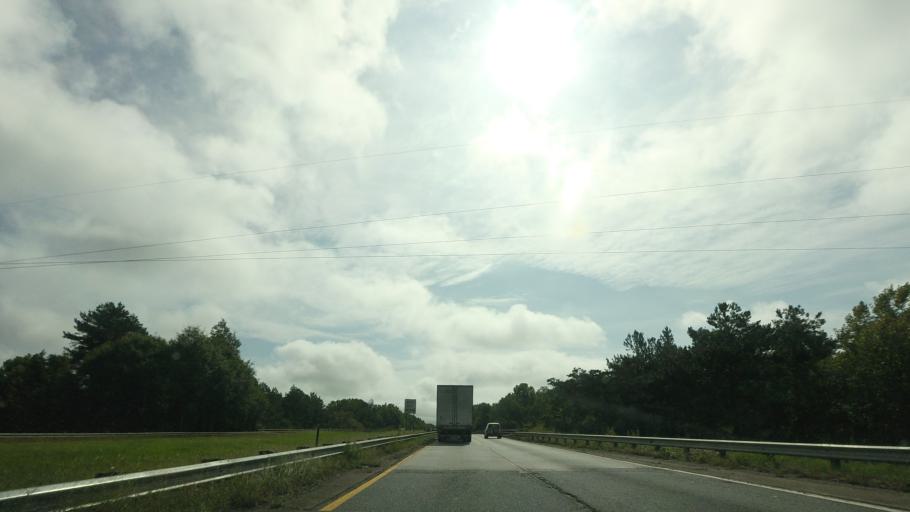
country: US
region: Georgia
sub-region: Bibb County
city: Macon
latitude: 32.8254
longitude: -83.5996
